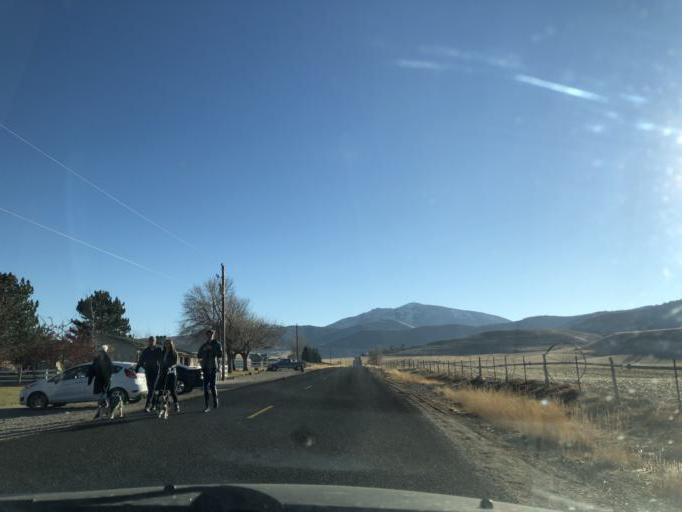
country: US
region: Utah
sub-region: Cache County
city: Wellsville
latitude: 41.6059
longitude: -111.9299
